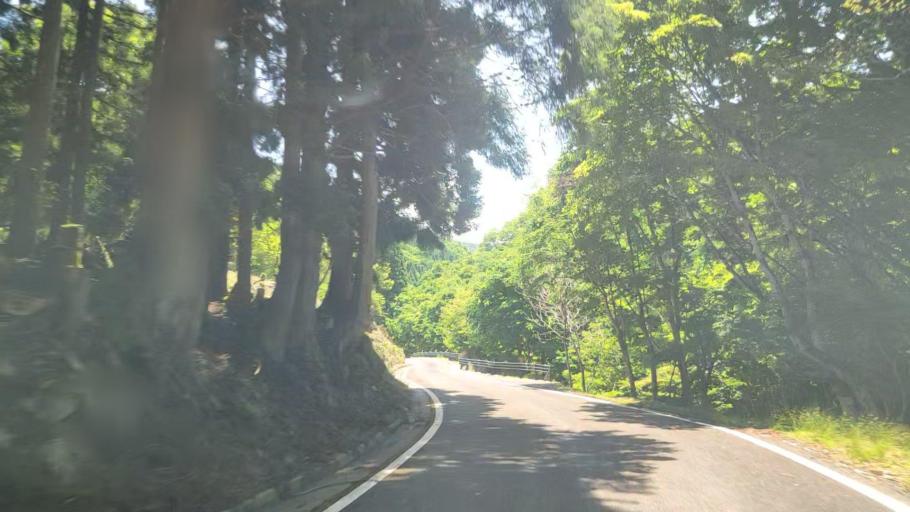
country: JP
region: Tottori
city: Tottori
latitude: 35.3824
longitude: 134.4892
